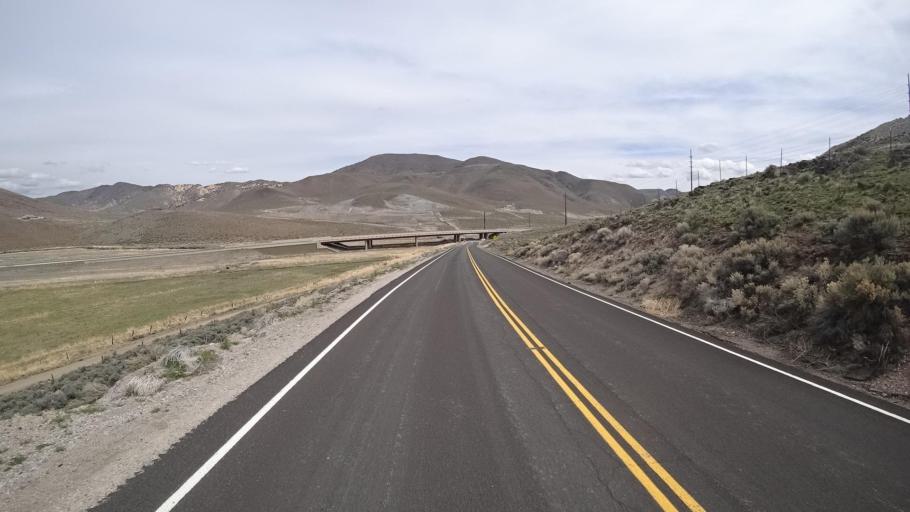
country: US
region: Nevada
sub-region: Washoe County
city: Sparks
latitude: 39.4664
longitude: -119.7330
